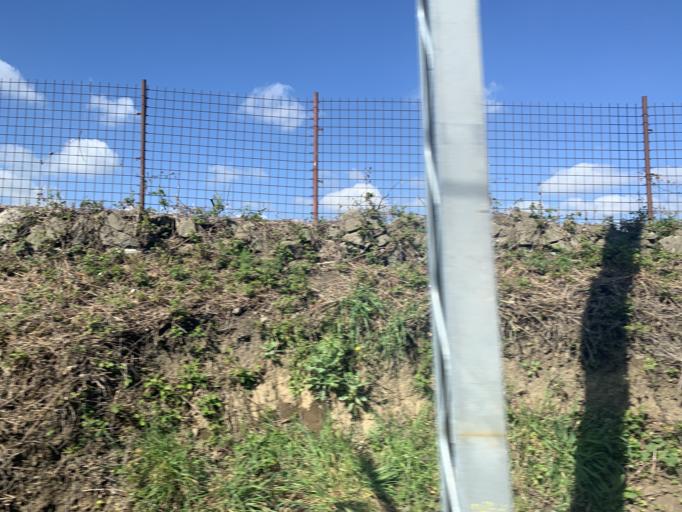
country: IT
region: Latium
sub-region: Citta metropolitana di Roma Capitale
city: Marino
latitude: 41.7824
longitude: 12.6431
